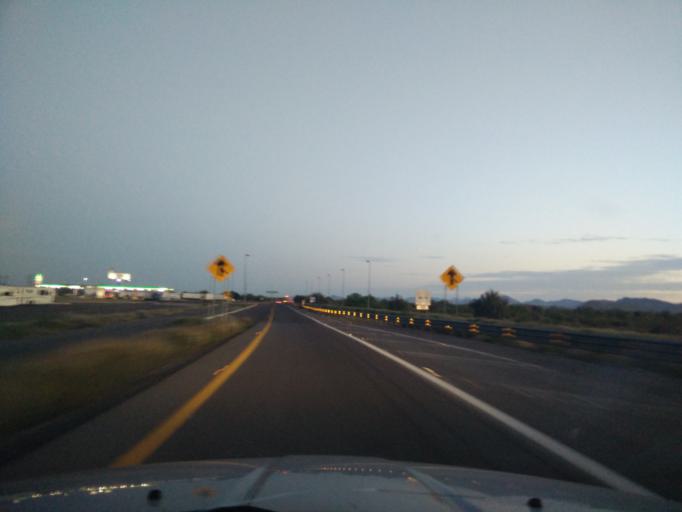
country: MX
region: Sonora
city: Heroica Guaymas
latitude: 28.0408
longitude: -110.9380
